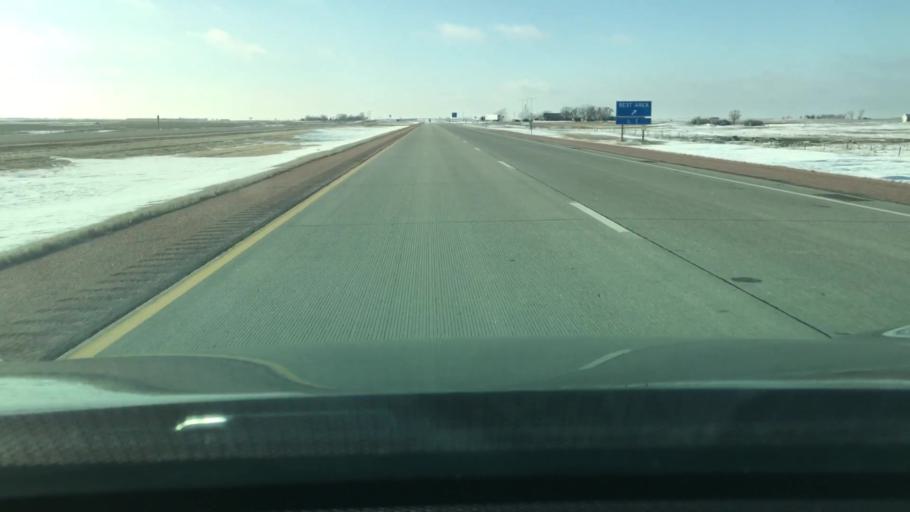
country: US
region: South Dakota
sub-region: Aurora County
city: Plankinton
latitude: 43.7085
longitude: -98.6084
